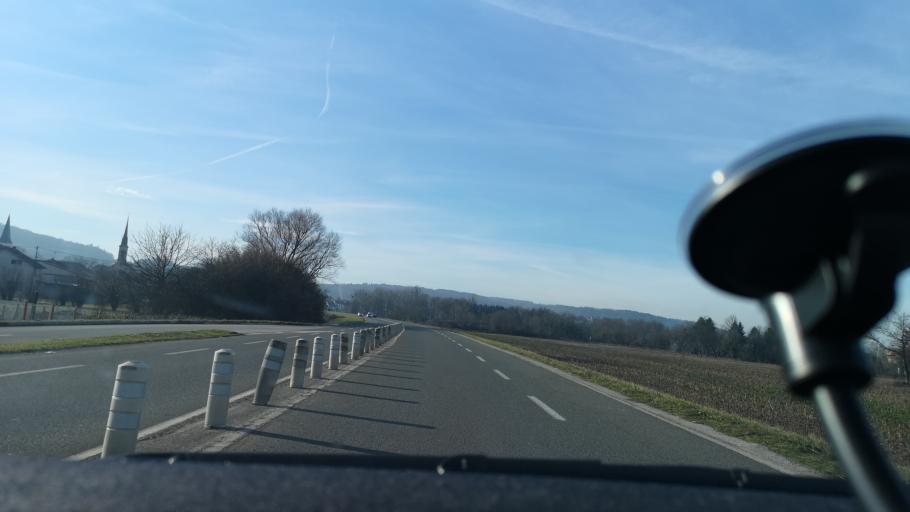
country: FR
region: Franche-Comte
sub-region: Departement du Doubs
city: Voujeaucourt
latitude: 47.4794
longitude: 6.7761
